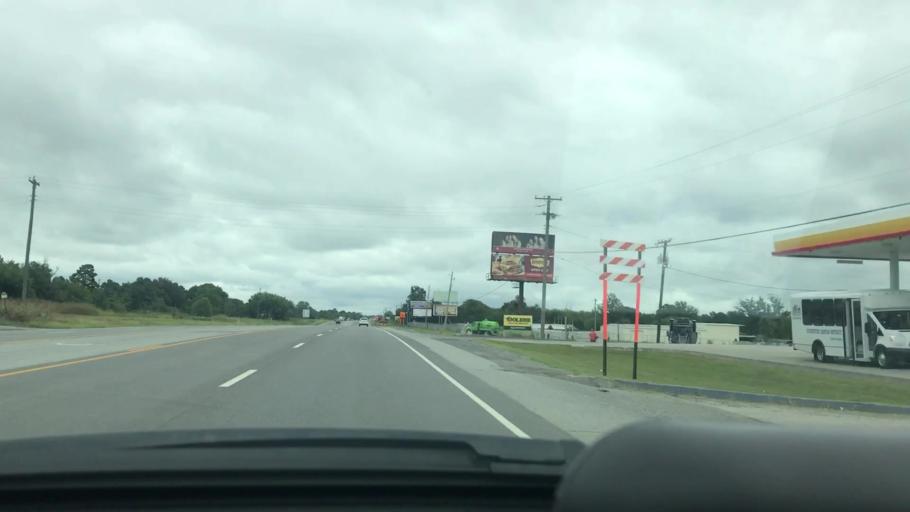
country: US
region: Oklahoma
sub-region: Pittsburg County
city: McAlester
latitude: 34.8741
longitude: -95.8003
